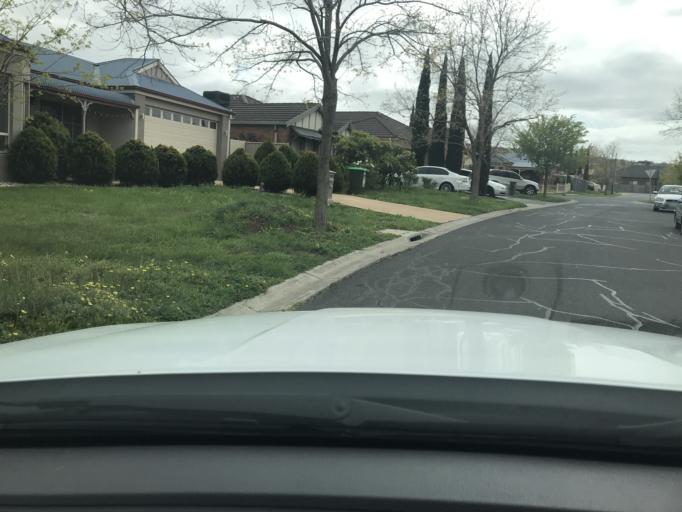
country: AU
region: Victoria
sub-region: Hume
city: Craigieburn
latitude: -37.5782
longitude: 144.9367
